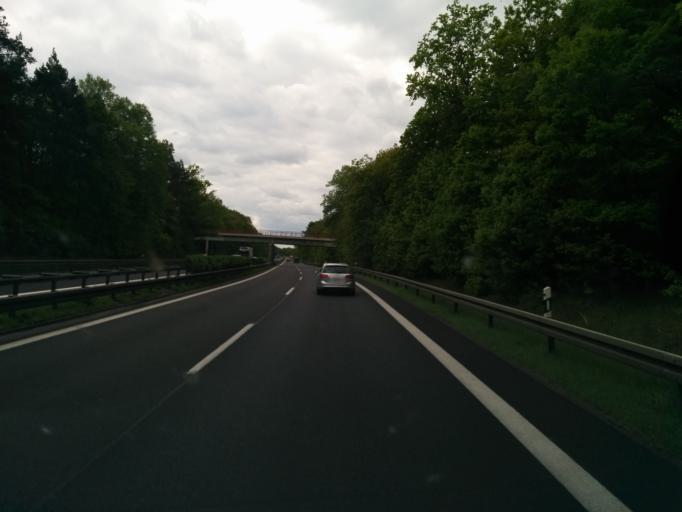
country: DE
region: Brandenburg
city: Gross Kreutz
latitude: 52.3916
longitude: 12.8294
